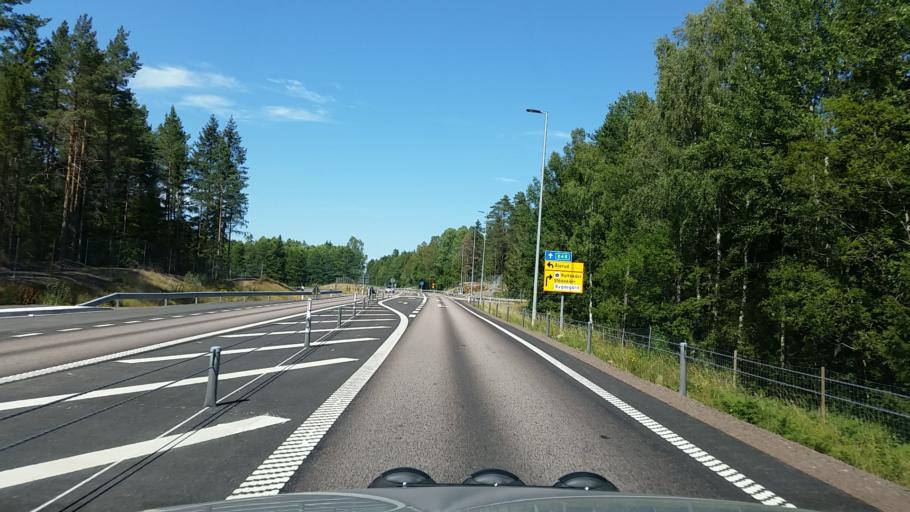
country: SE
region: Vaestra Goetaland
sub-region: Amals Kommun
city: Amal
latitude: 58.9381
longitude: 12.6004
